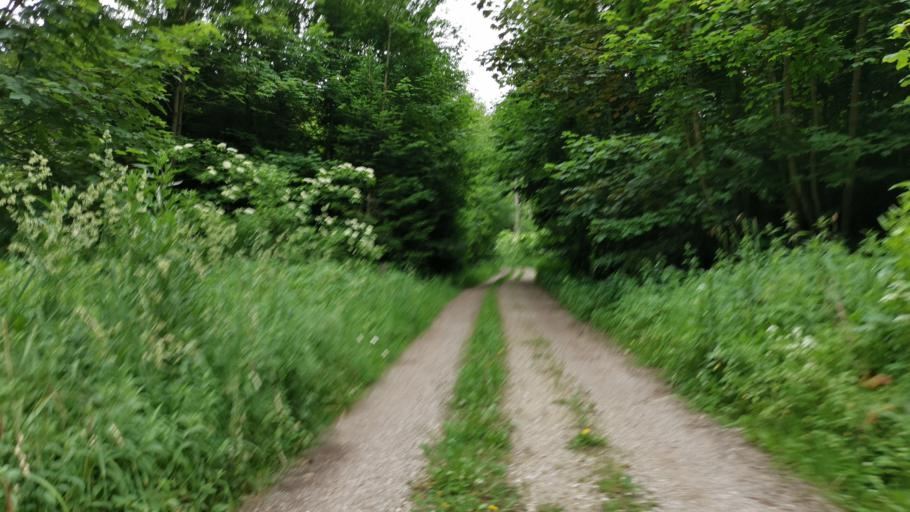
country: DE
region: Bavaria
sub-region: Upper Bavaria
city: Schaftlarn
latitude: 48.0009
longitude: 11.4392
